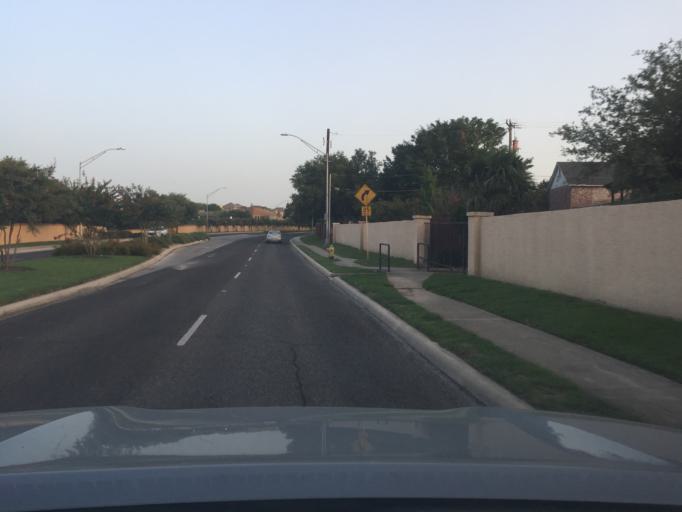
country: US
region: Texas
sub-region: Bexar County
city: Hollywood Park
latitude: 29.6539
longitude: -98.4954
